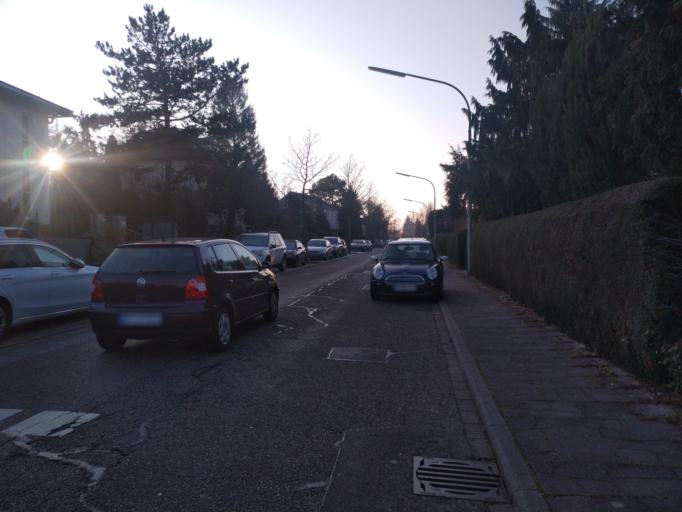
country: DE
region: Baden-Wuerttemberg
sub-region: Karlsruhe Region
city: Pforzheim
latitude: 48.8868
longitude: 8.6842
